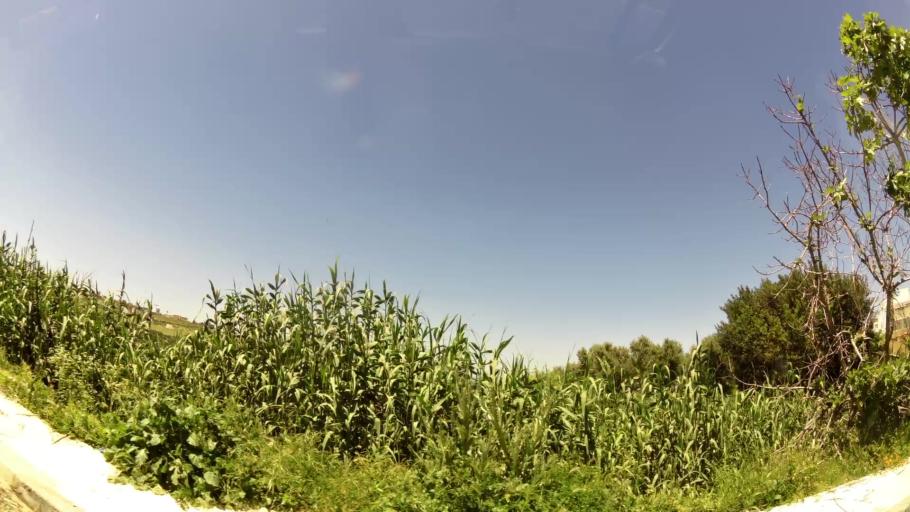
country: MA
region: Meknes-Tafilalet
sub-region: Meknes
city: Meknes
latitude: 33.9084
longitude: -5.5642
